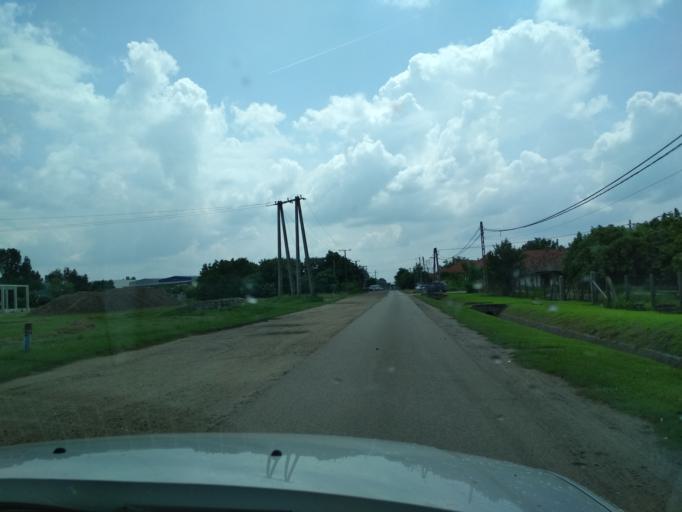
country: HU
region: Pest
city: Nagykata
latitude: 47.4022
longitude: 19.7602
